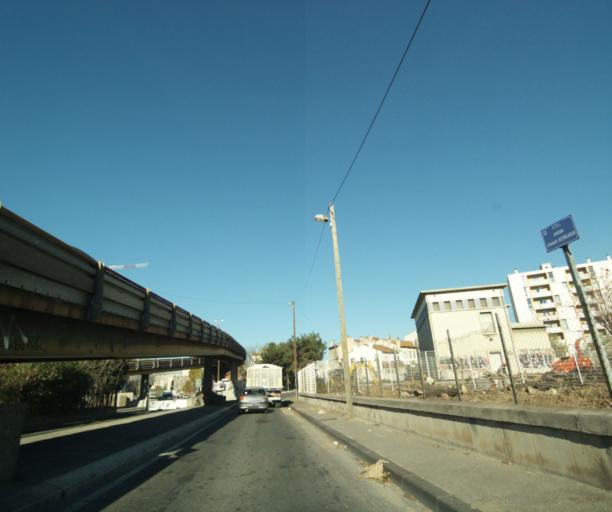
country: FR
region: Provence-Alpes-Cote d'Azur
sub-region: Departement des Bouches-du-Rhone
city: Marseille 10
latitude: 43.2805
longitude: 5.4271
